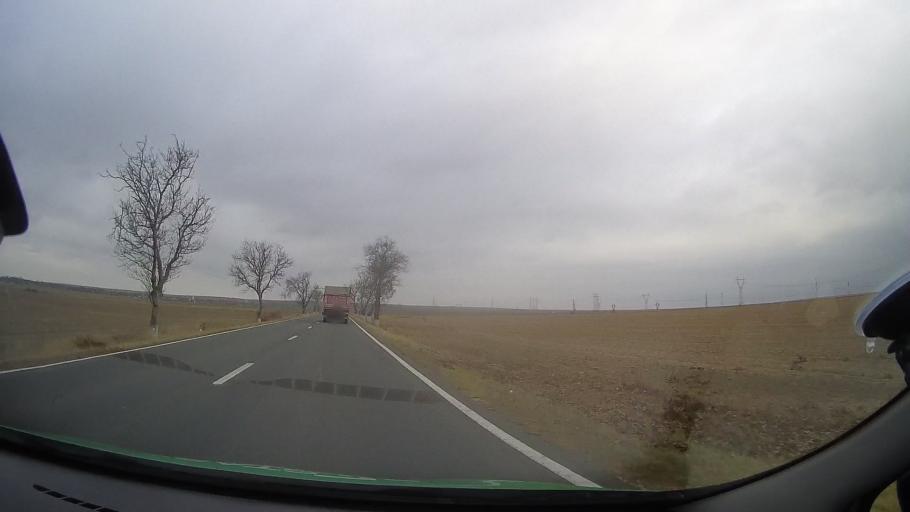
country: RO
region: Constanta
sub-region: Comuna Castelu
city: Castelu
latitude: 44.2503
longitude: 28.3569
